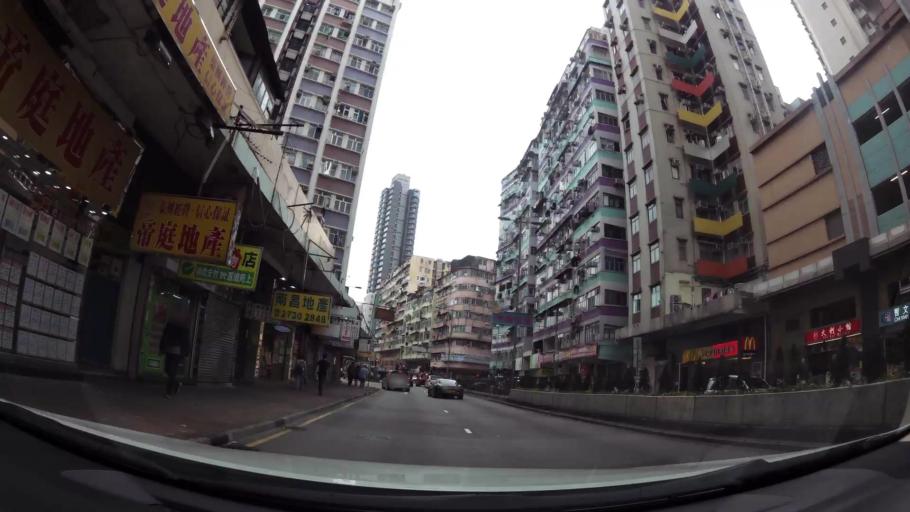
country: HK
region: Sham Shui Po
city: Sham Shui Po
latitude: 22.3299
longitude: 114.1661
